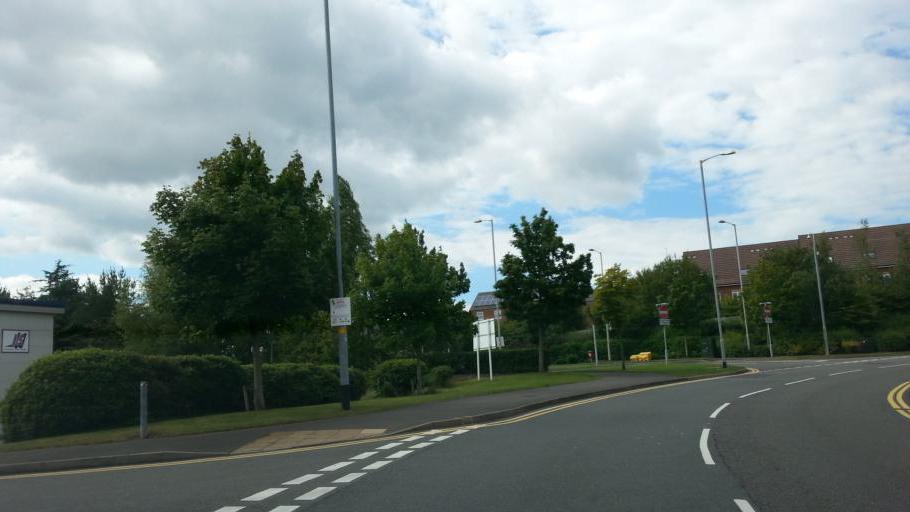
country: GB
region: England
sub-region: Coventry
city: Keresley
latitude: 52.4571
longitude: -1.5322
